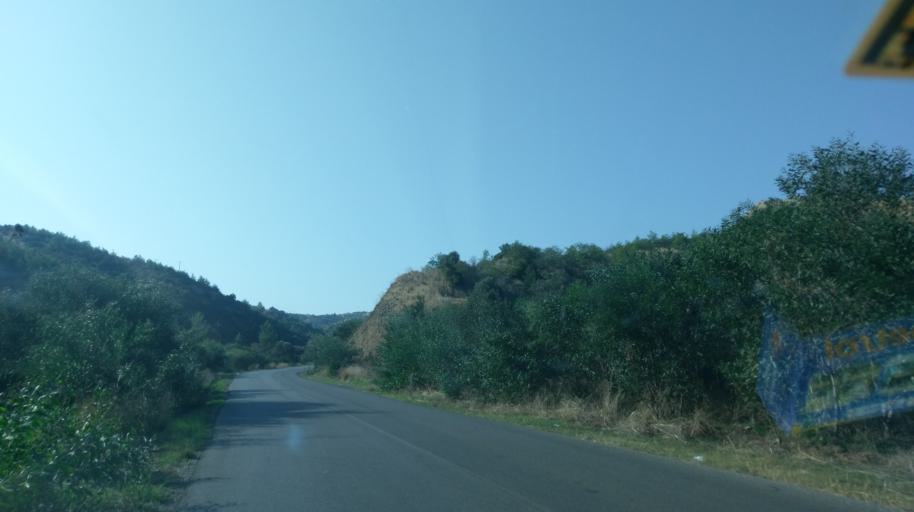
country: CY
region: Lefkosia
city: Lefka
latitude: 35.1521
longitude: 32.7803
